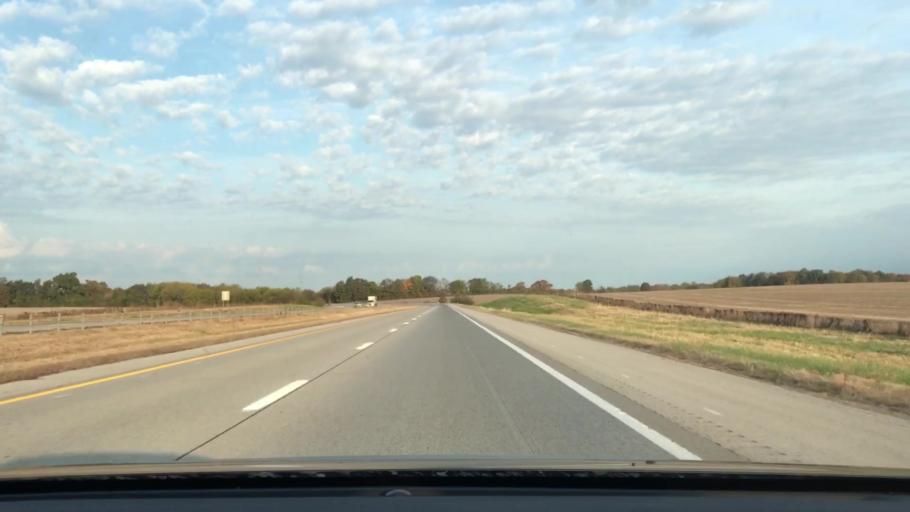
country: US
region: Kentucky
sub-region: Christian County
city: Hopkinsville
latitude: 36.8109
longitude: -87.6221
